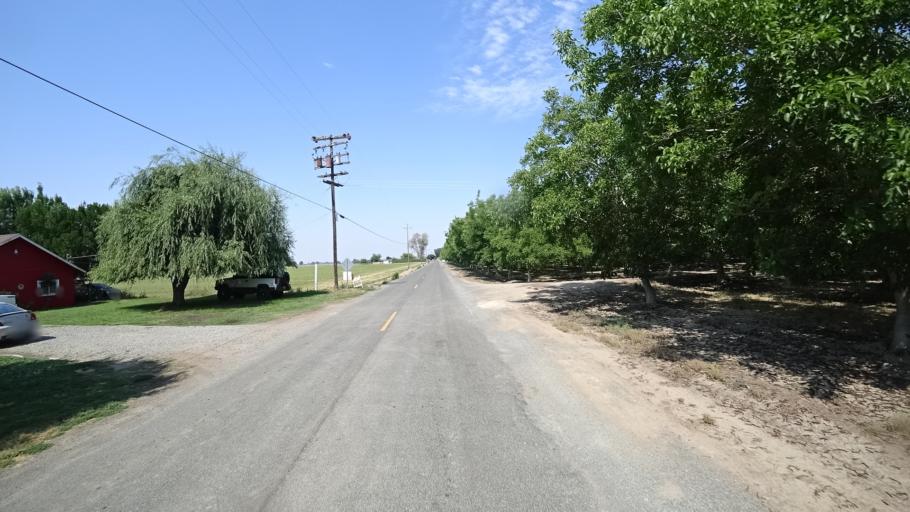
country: US
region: California
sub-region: Fresno County
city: Laton
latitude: 36.3948
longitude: -119.7643
